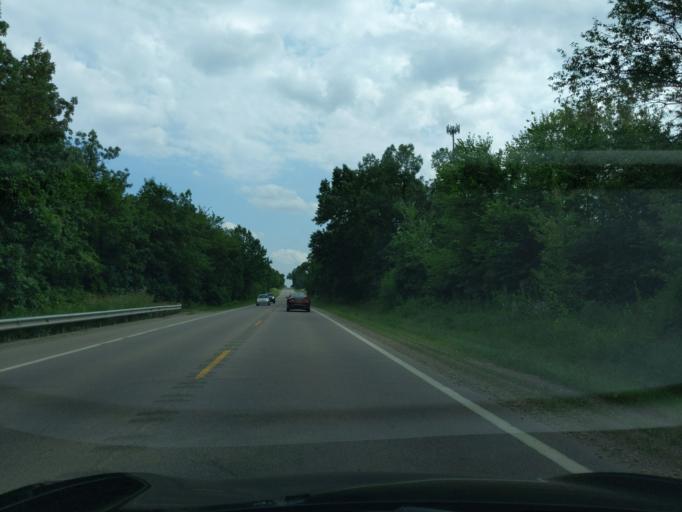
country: US
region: Michigan
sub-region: Eaton County
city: Eaton Rapids
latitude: 42.4427
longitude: -84.6496
